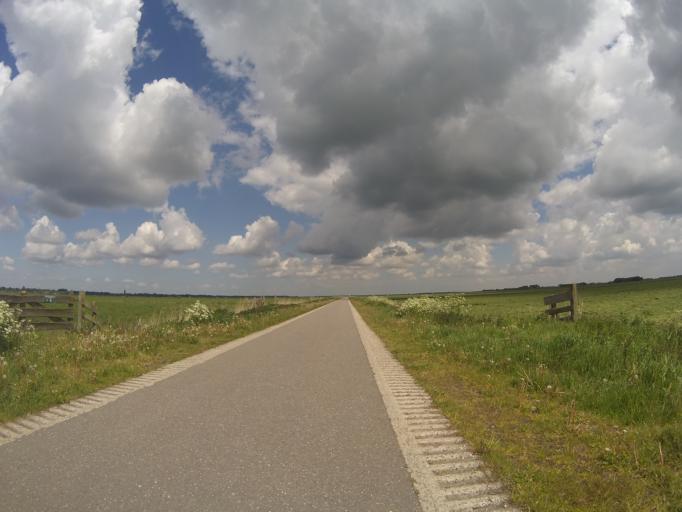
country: NL
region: Utrecht
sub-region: Gemeente Baarn
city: Baarn
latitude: 52.2334
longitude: 5.2850
